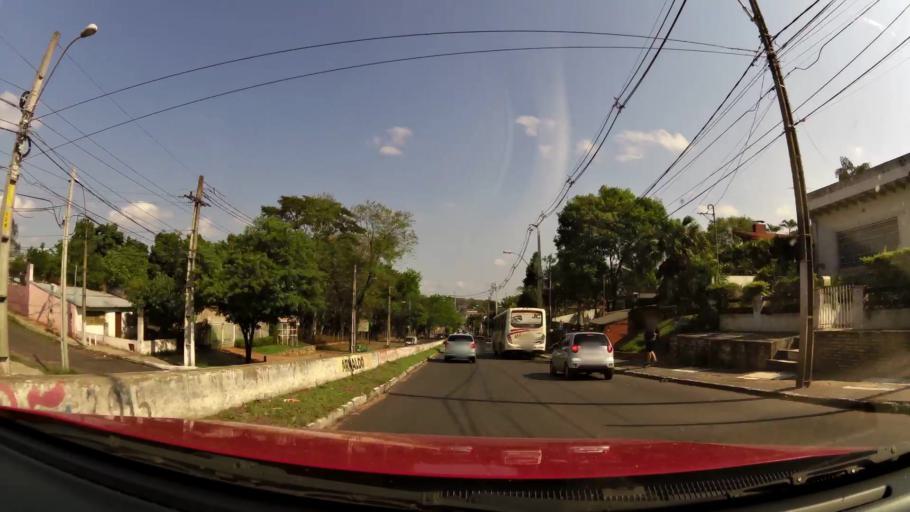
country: PY
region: Asuncion
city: Asuncion
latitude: -25.3106
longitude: -57.6314
